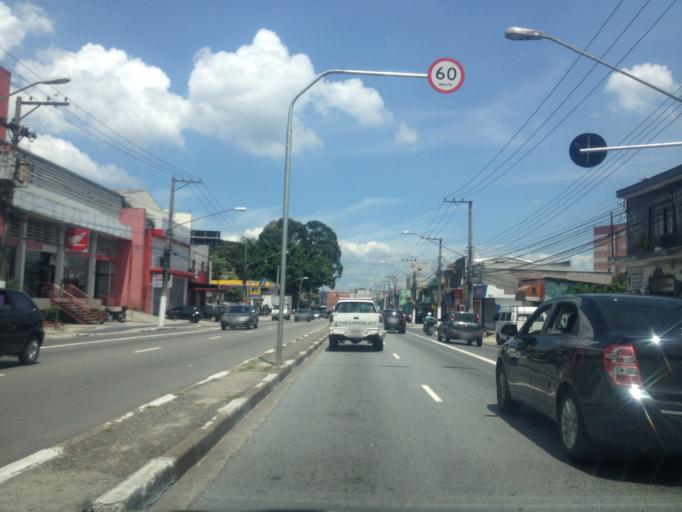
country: BR
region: Sao Paulo
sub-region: Diadema
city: Diadema
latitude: -23.6773
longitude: -46.6816
